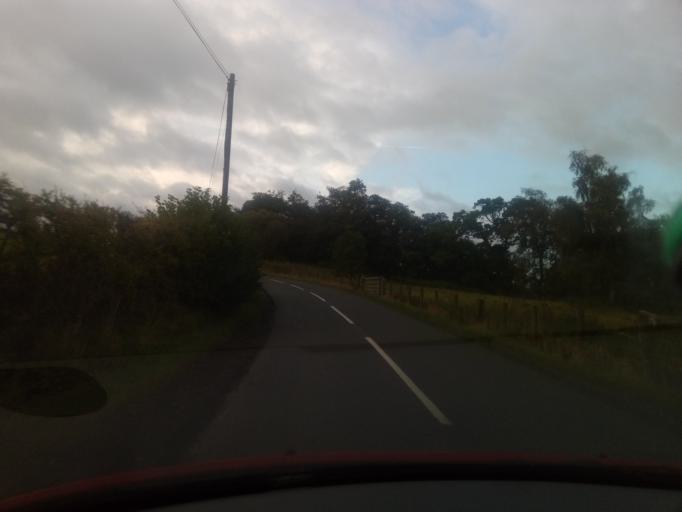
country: GB
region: Scotland
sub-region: The Scottish Borders
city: Jedburgh
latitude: 55.4198
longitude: -2.6311
